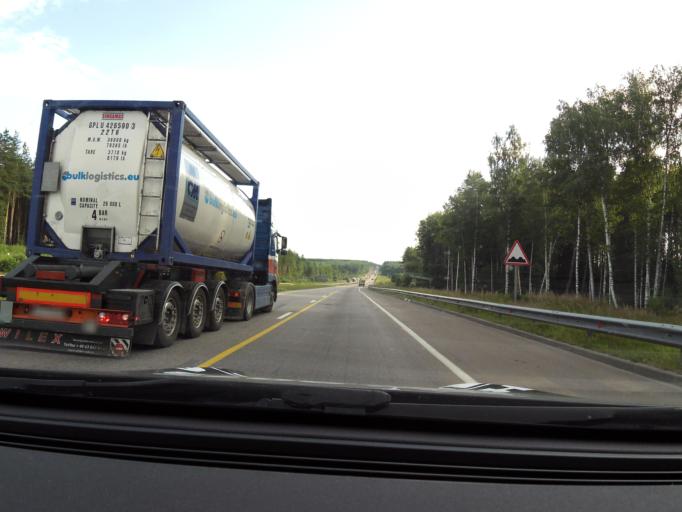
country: RU
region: Vladimir
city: Sudogda
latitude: 56.1310
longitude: 40.8777
